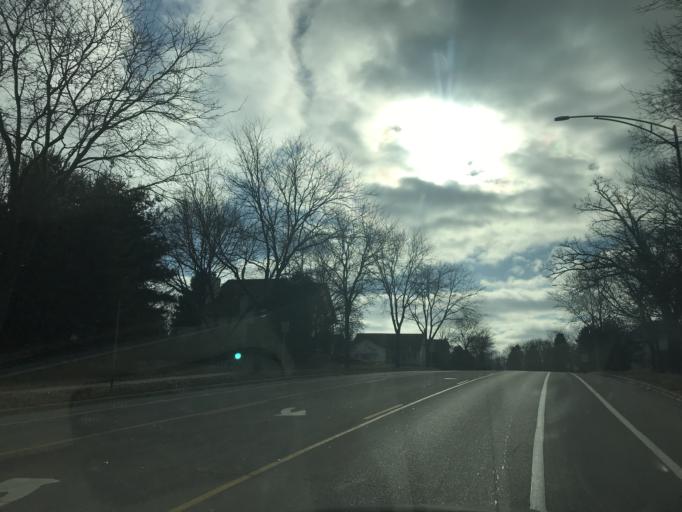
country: US
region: Wisconsin
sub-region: Dane County
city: Monona
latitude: 43.1190
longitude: -89.2978
